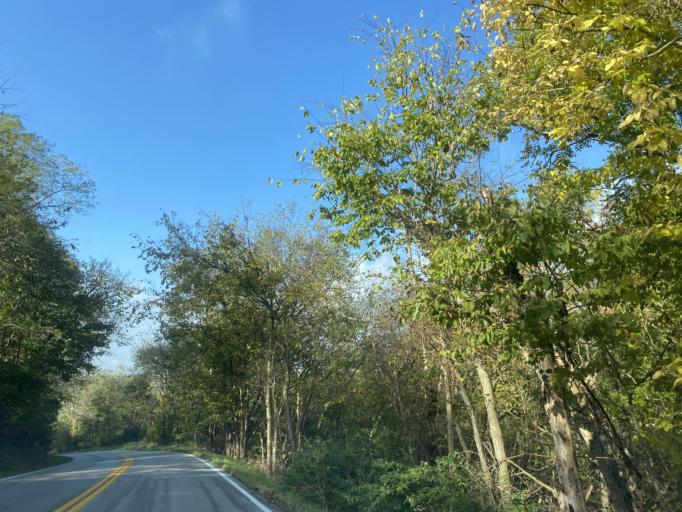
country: US
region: Kentucky
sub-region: Pendleton County
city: Falmouth
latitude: 38.6828
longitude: -84.3180
